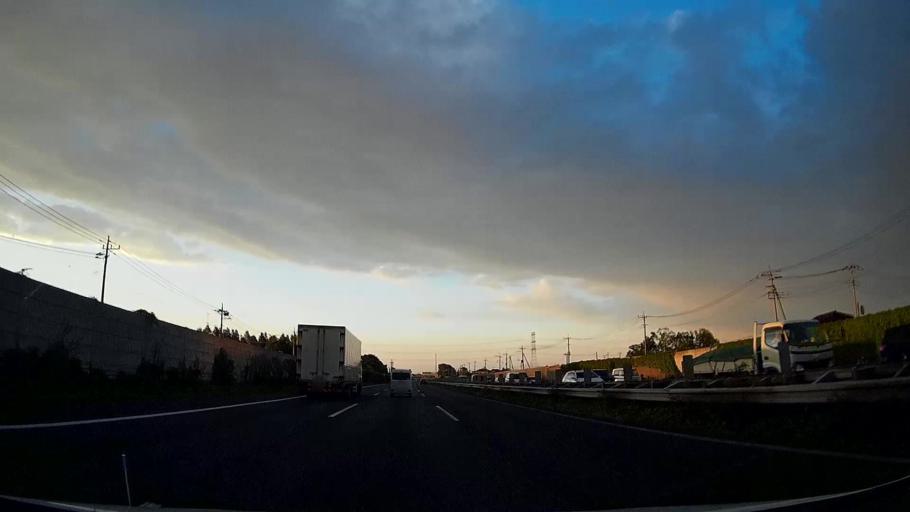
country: JP
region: Saitama
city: Kazo
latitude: 36.0963
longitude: 139.6379
